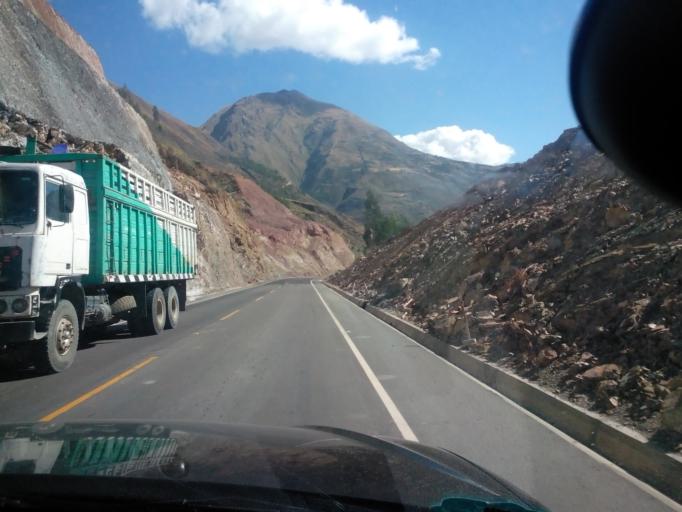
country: PE
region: Cusco
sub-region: Provincia de Quispicanchis
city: Huaro
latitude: -13.6777
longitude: -71.6311
